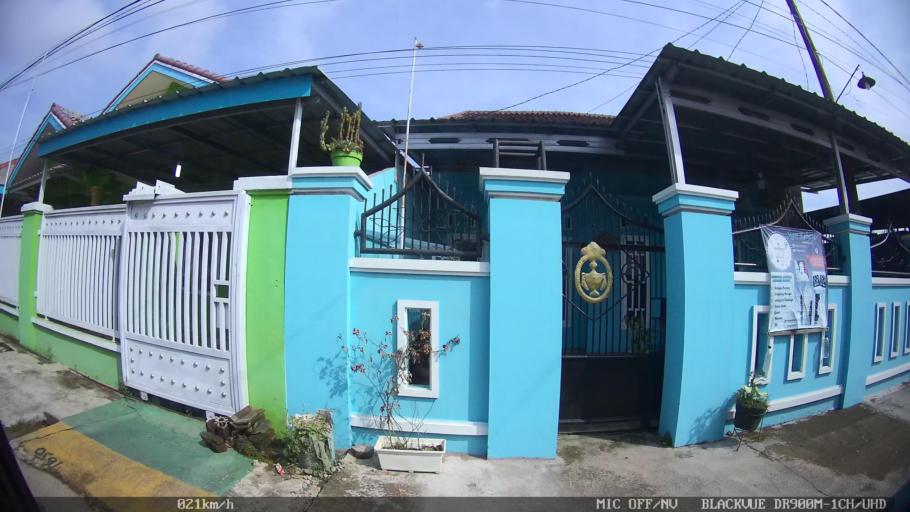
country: ID
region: Lampung
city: Kedaton
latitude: -5.3818
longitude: 105.2962
